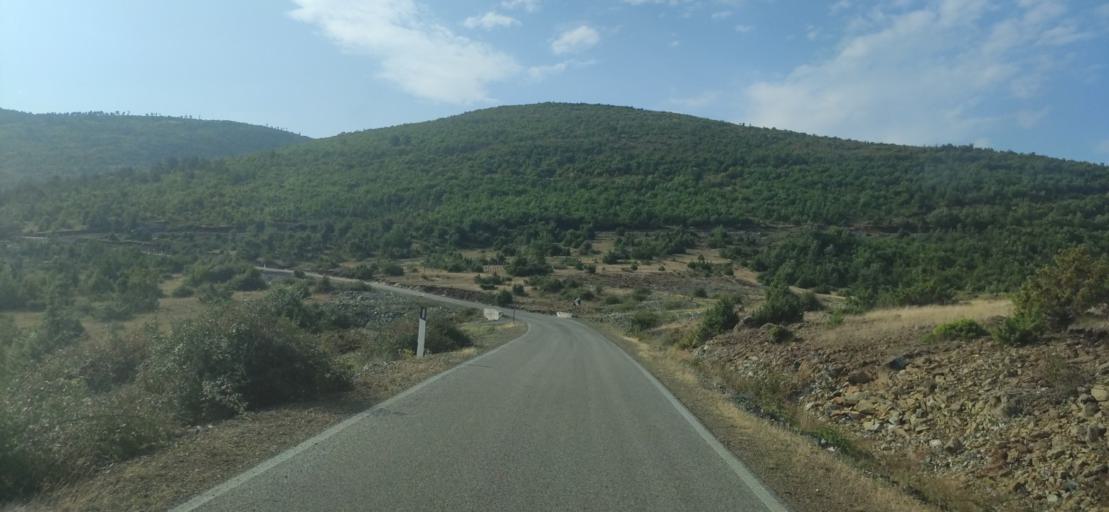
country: AL
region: Shkoder
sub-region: Rrethi i Pukes
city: Iballe
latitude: 42.1788
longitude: 20.0016
